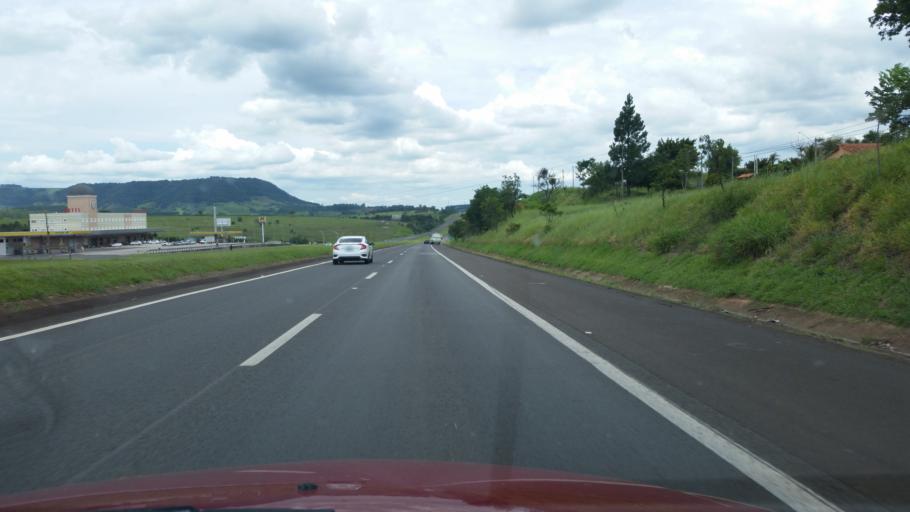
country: BR
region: Sao Paulo
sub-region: Itatinga
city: Itatinga
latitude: -23.1465
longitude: -48.4042
